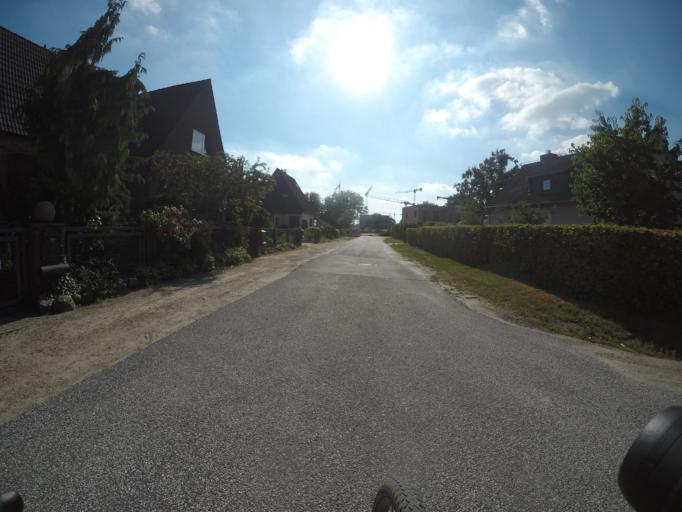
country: DE
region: Schleswig-Holstein
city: Glinde
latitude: 53.5136
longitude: 10.2035
